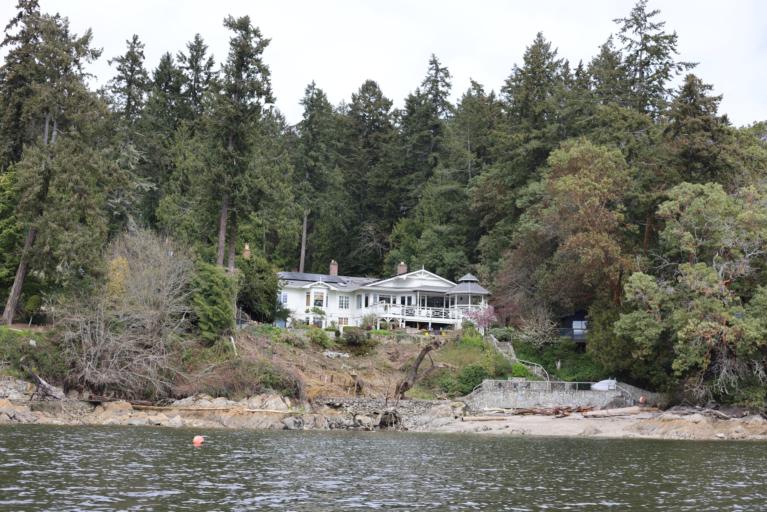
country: CA
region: British Columbia
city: North Saanich
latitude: 48.5946
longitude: -123.4738
